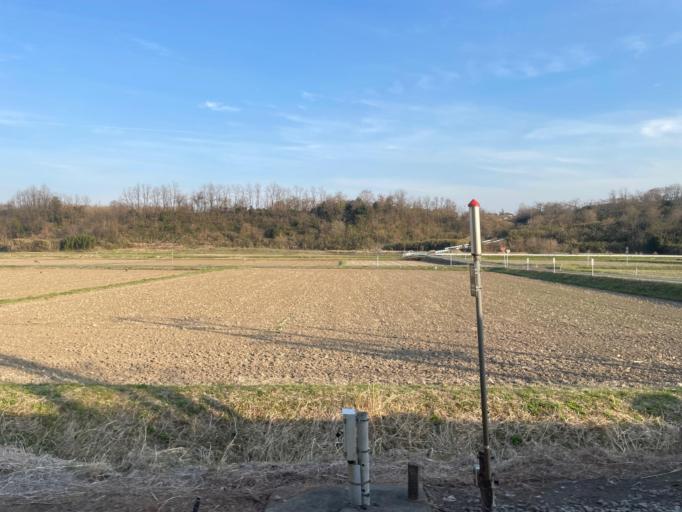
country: JP
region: Gunma
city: Annaka
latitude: 36.3076
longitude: 138.8758
